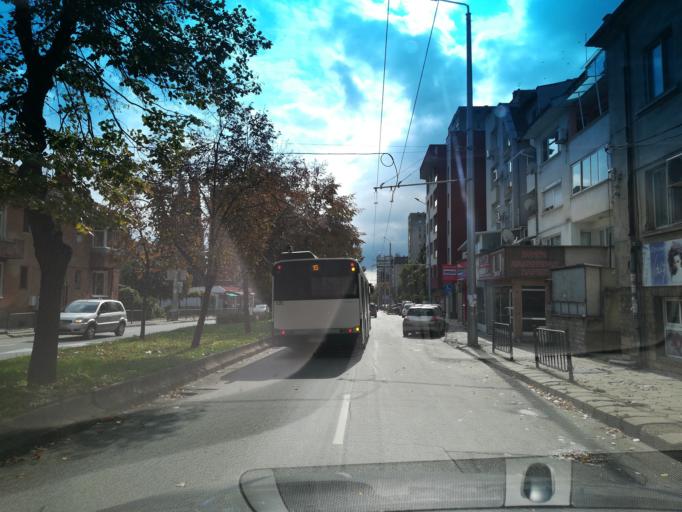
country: BG
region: Stara Zagora
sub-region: Obshtina Stara Zagora
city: Stara Zagora
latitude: 42.4326
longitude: 25.6324
